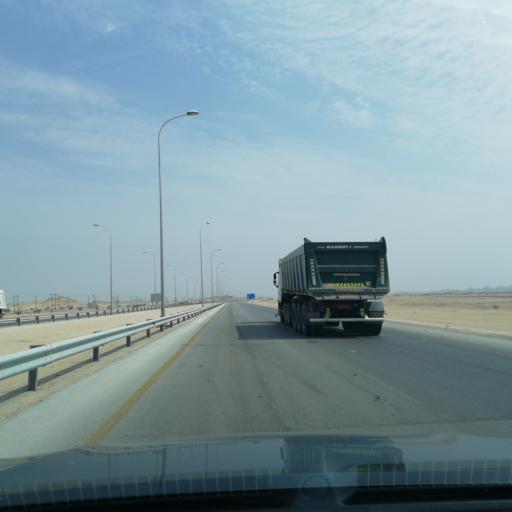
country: OM
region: Zufar
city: Salalah
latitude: 17.4757
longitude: 54.0504
